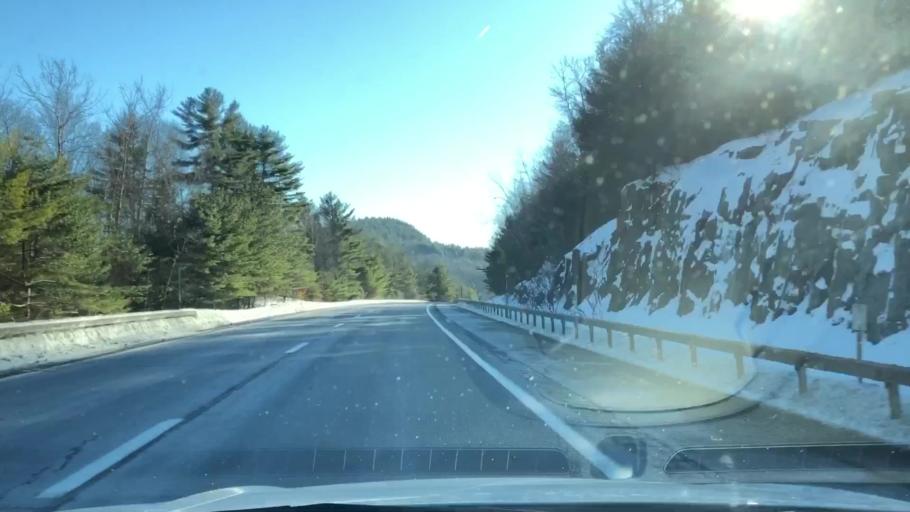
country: US
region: New York
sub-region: Warren County
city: Warrensburg
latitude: 43.7668
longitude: -73.8039
